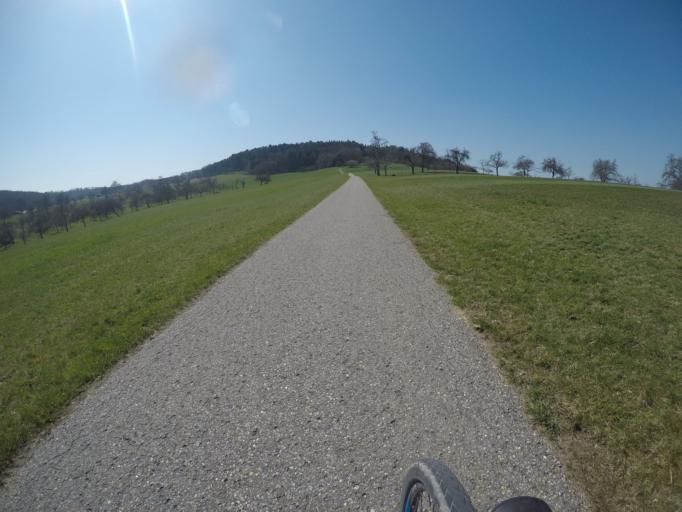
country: DE
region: Baden-Wuerttemberg
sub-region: Karlsruhe Region
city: Gechingen
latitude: 48.6928
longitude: 8.8112
